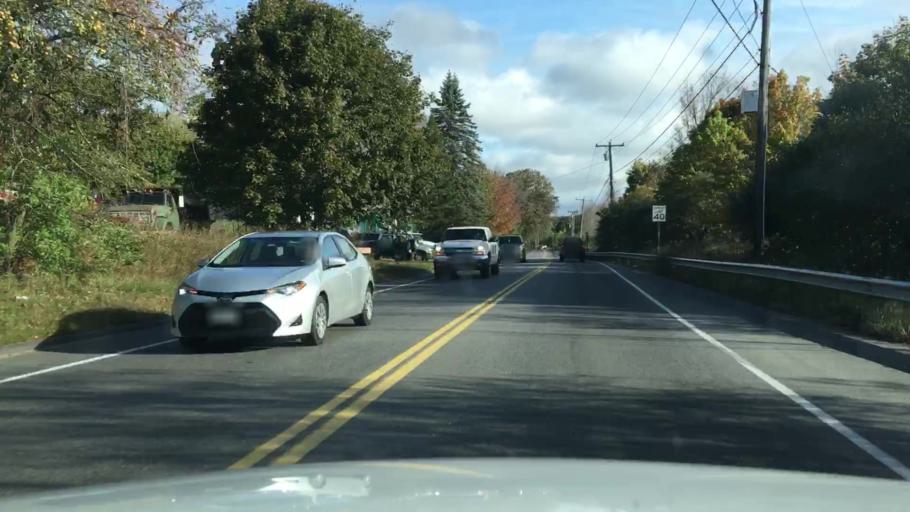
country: US
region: Maine
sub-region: Knox County
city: Rockland
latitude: 44.1103
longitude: -69.1342
